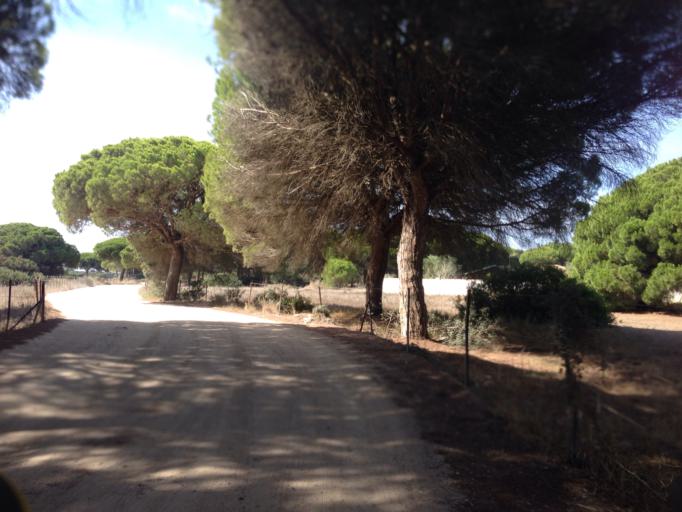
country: ES
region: Andalusia
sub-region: Provincia de Cadiz
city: Chiclana de la Frontera
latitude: 36.3780
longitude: -6.1313
